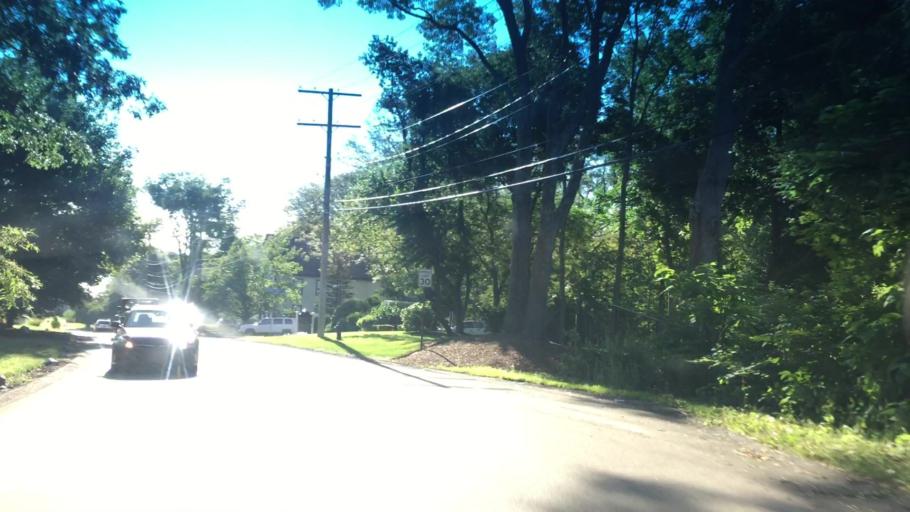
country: US
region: Massachusetts
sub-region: Norfolk County
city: Walpole
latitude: 42.1424
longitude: -71.2638
